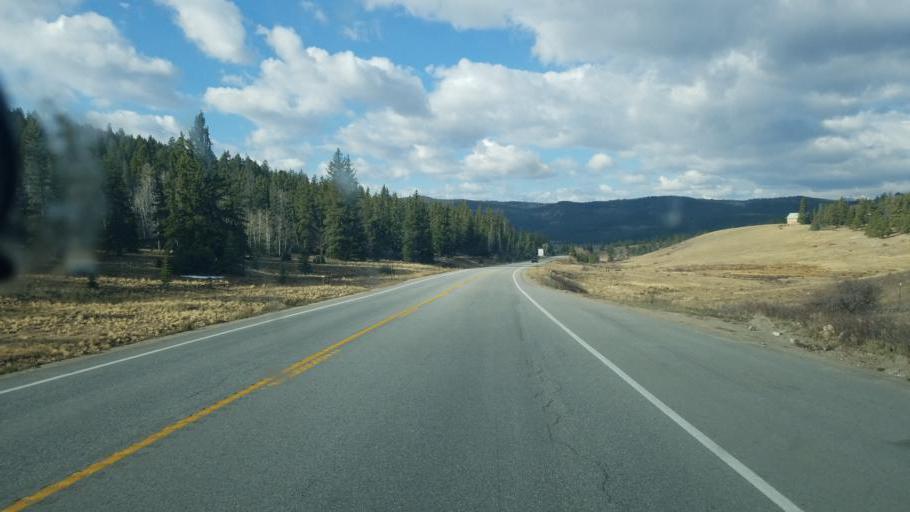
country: US
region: Colorado
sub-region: Chaffee County
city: Buena Vista
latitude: 38.9079
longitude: -105.9794
